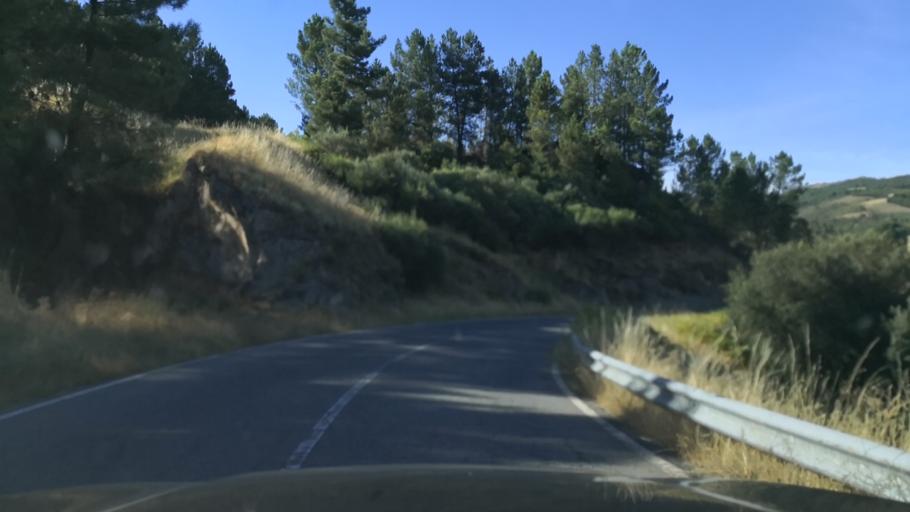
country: PT
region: Vila Real
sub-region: Murca
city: Murca
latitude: 41.4060
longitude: -7.4685
